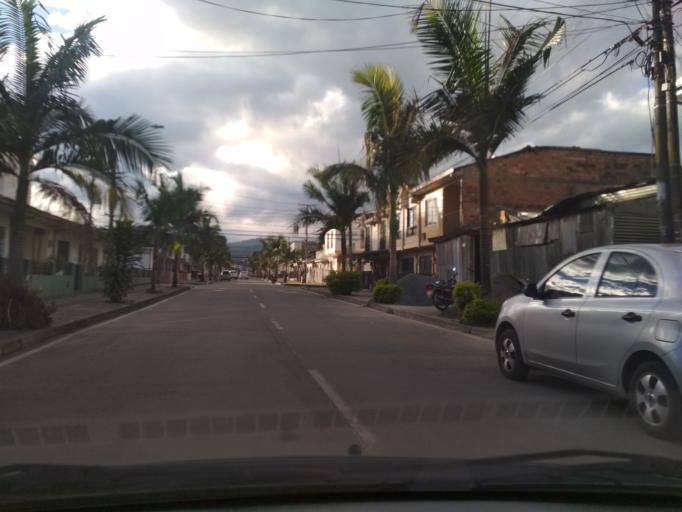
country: CO
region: Cauca
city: Popayan
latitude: 2.4421
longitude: -76.6137
